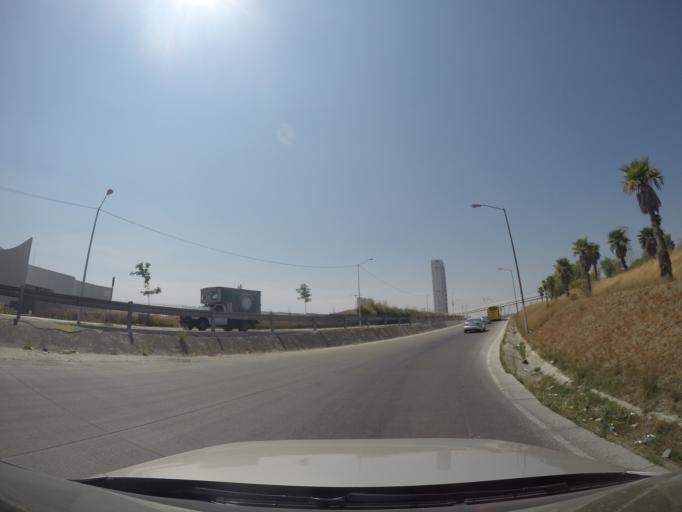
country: MX
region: Puebla
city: Tlazcalancingo
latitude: 19.0188
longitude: -98.2477
